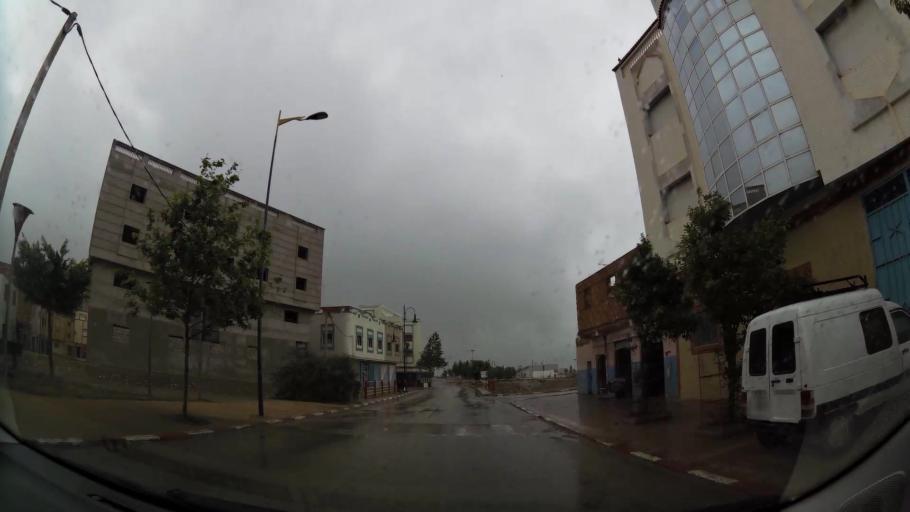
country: MA
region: Taza-Al Hoceima-Taounate
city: Imzourene
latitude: 35.1540
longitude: -3.8490
